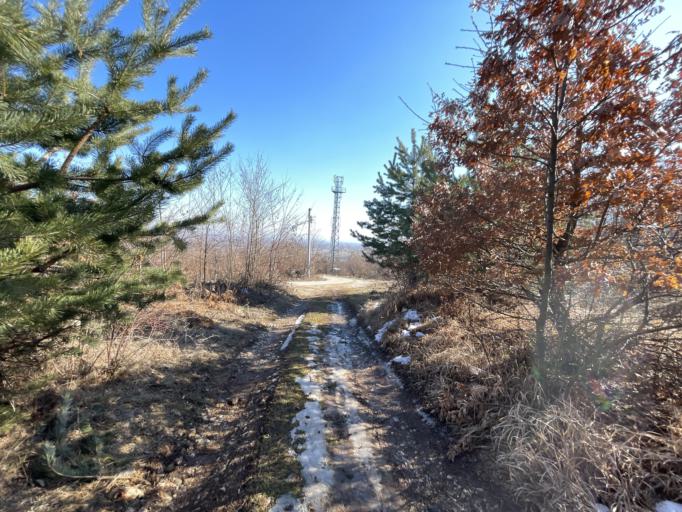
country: XK
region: Gjakova
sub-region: Komuna e Decanit
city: Strellc i Eperm
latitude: 42.6013
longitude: 20.2847
